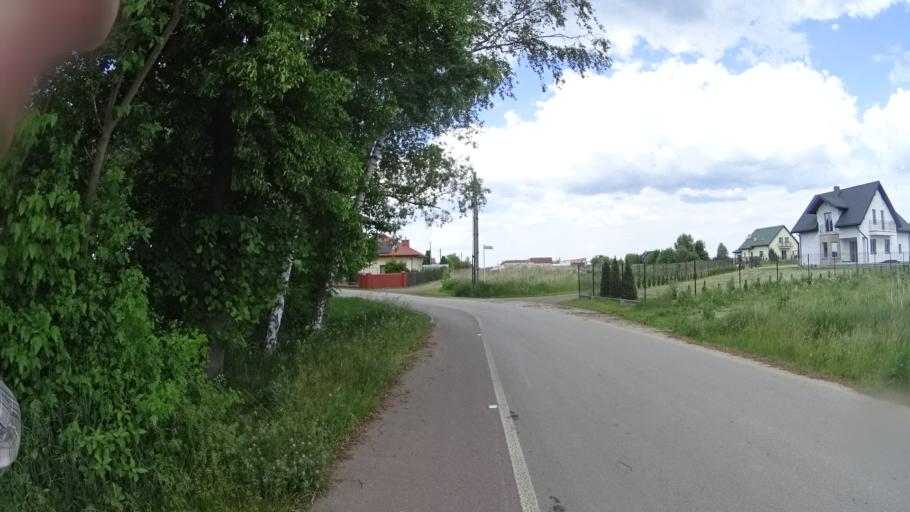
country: PL
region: Masovian Voivodeship
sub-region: Powiat piaseczynski
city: Tarczyn
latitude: 52.0069
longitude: 20.8319
